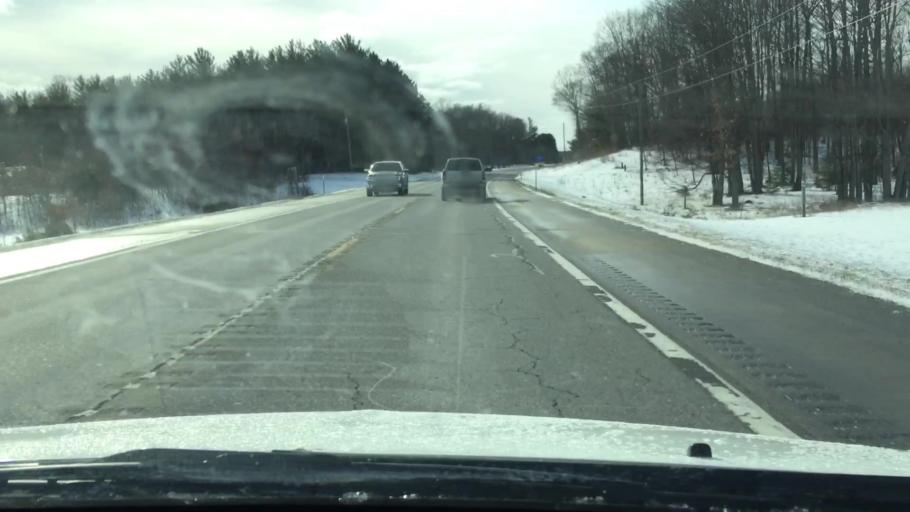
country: US
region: Michigan
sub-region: Wexford County
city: Manton
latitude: 44.5895
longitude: -85.3415
